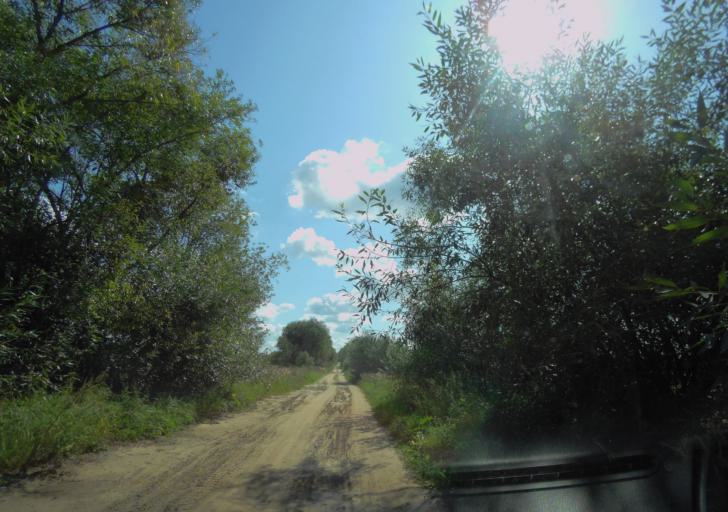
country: BY
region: Minsk
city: Zyembin
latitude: 54.4136
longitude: 28.3764
